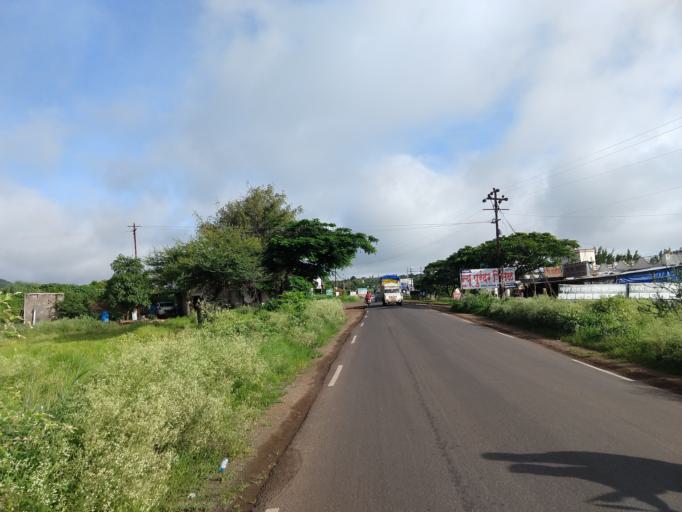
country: IN
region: Maharashtra
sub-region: Pune Division
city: Khed
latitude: 18.3957
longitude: 73.9155
